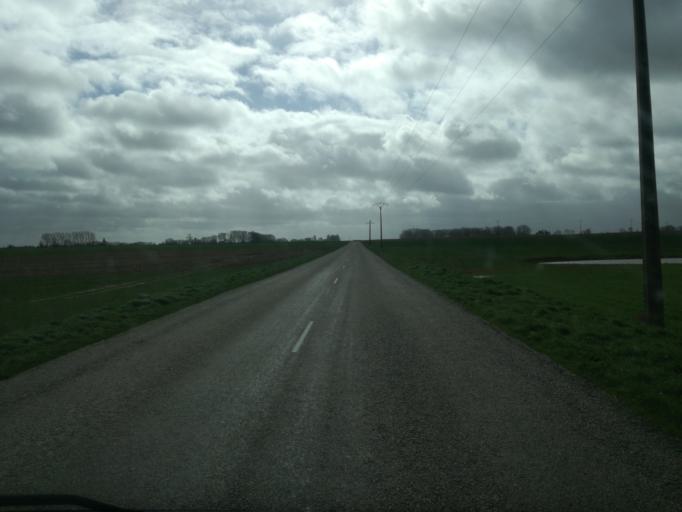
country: FR
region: Haute-Normandie
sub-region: Departement de la Seine-Maritime
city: Valliquerville
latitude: 49.6055
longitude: 0.6670
